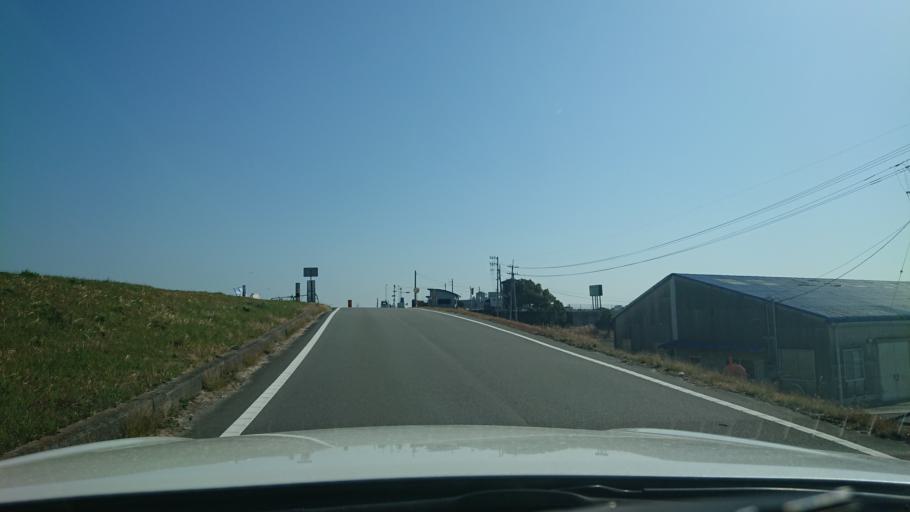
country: JP
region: Tokushima
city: Anan
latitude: 33.9380
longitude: 134.6196
